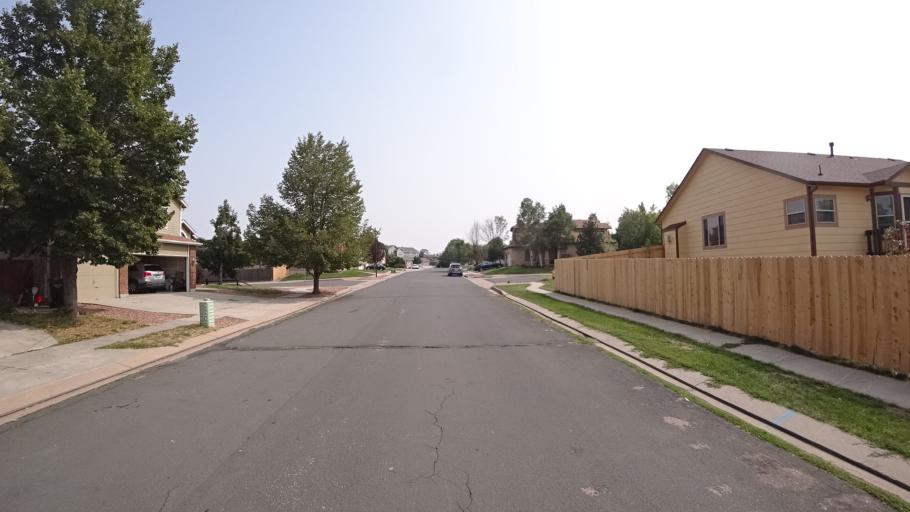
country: US
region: Colorado
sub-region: El Paso County
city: Cimarron Hills
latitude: 38.9176
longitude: -104.7309
